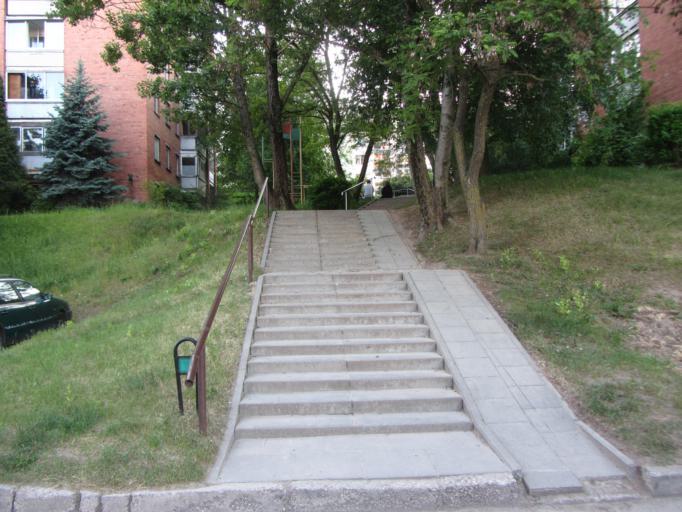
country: LT
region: Vilnius County
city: Seskine
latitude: 54.7278
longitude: 25.2756
